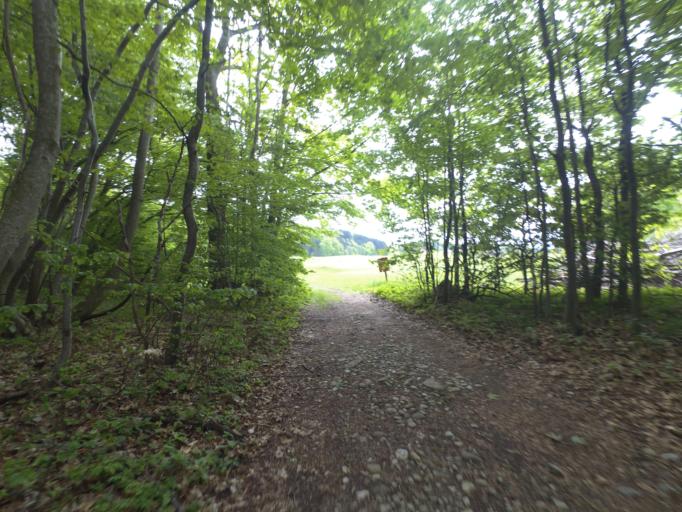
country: AT
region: Salzburg
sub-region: Politischer Bezirk Salzburg-Umgebung
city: Schleedorf
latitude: 47.9813
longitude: 13.1410
